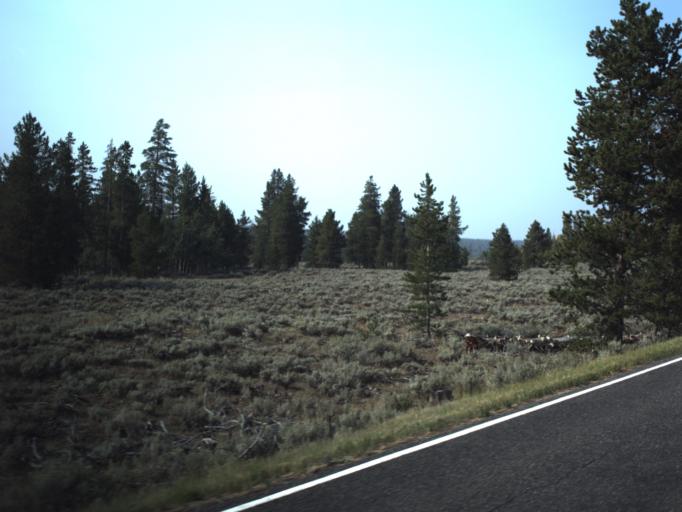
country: US
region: Wyoming
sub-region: Uinta County
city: Evanston
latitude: 40.8748
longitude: -110.8319
